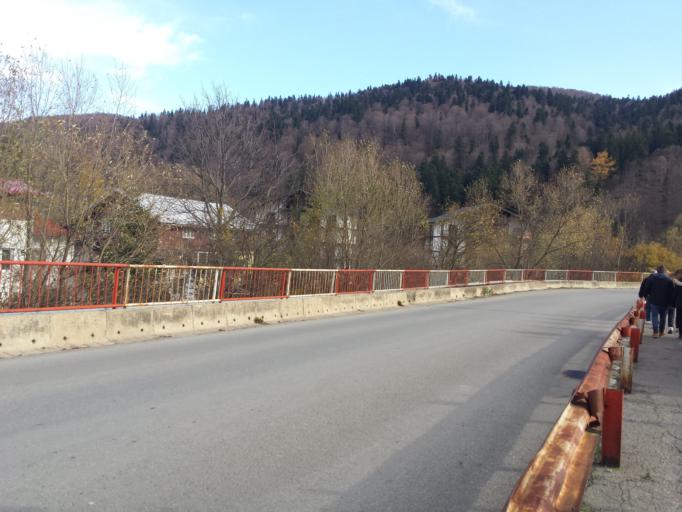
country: RO
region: Prahova
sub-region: Oras Busteni
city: Busteni
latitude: 45.4161
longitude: 25.5397
